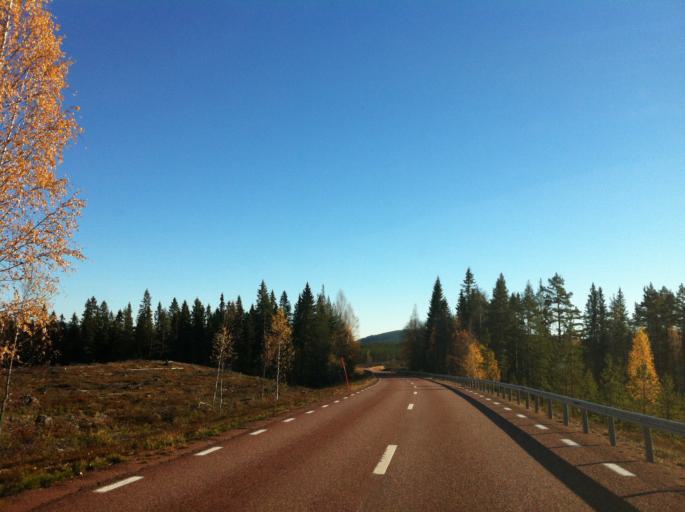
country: SE
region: Dalarna
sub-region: Alvdalens Kommun
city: AElvdalen
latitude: 61.3291
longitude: 13.5994
